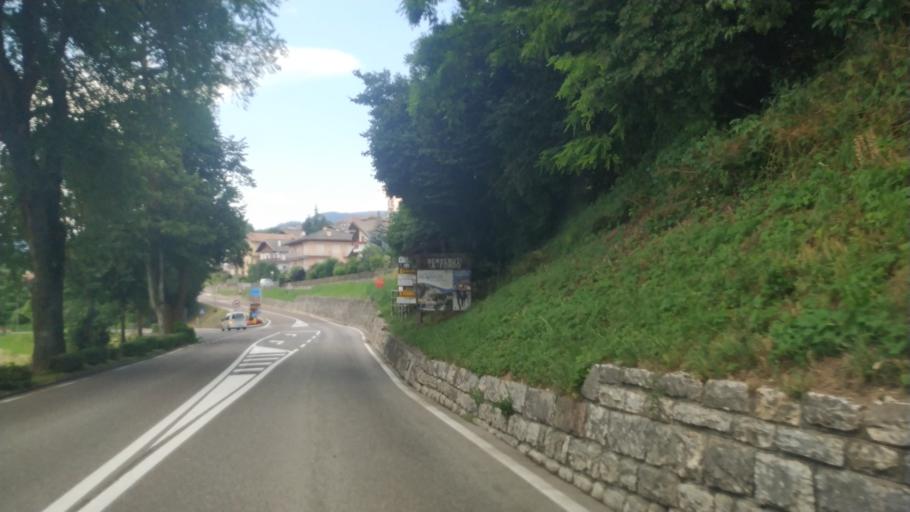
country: IT
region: Trentino-Alto Adige
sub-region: Provincia di Trento
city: Malosco
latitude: 46.4313
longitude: 11.1405
